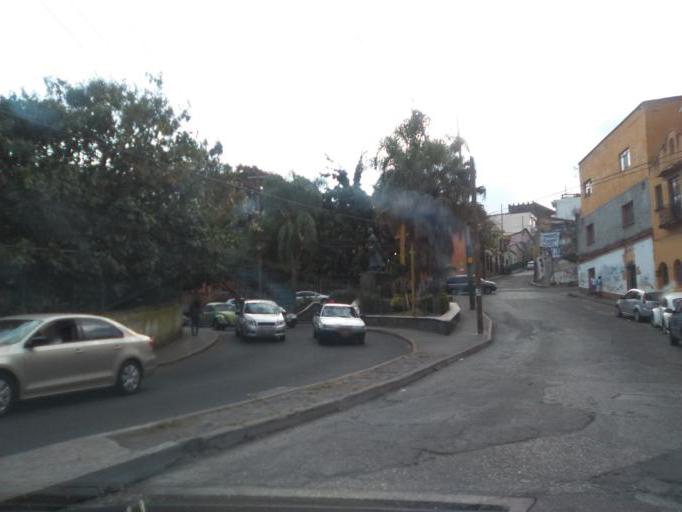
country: MX
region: Morelos
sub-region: Cuernavaca
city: Cuernavaca
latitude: 18.9221
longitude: -99.2314
